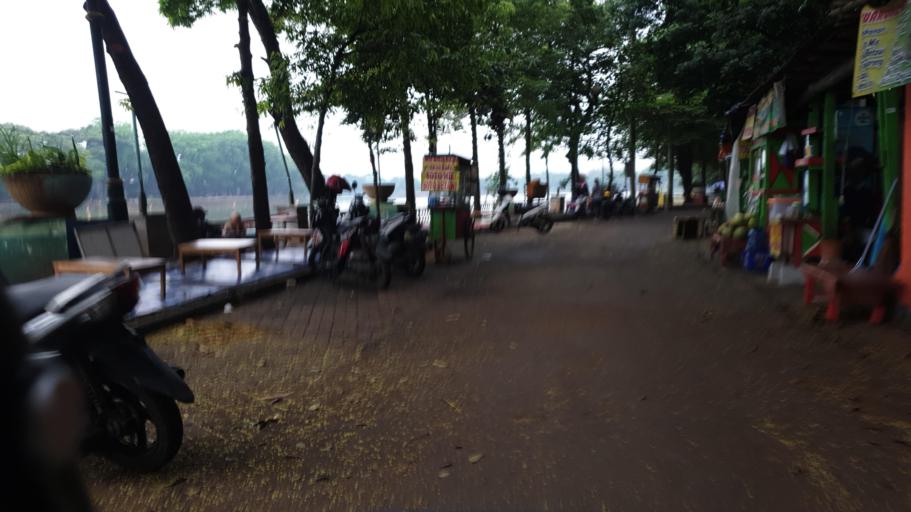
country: ID
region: West Java
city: Depok
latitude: -6.3403
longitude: 106.8247
